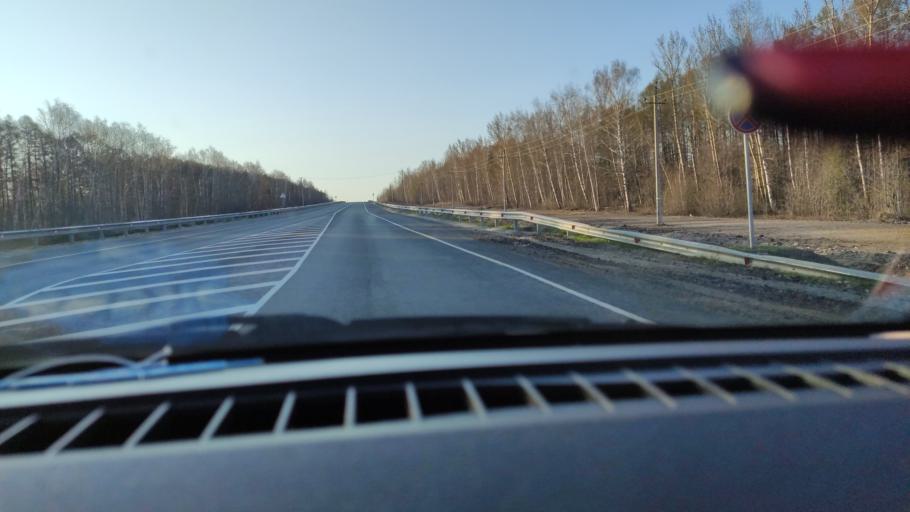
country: RU
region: Saratov
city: Shikhany
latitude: 52.1484
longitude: 47.1928
